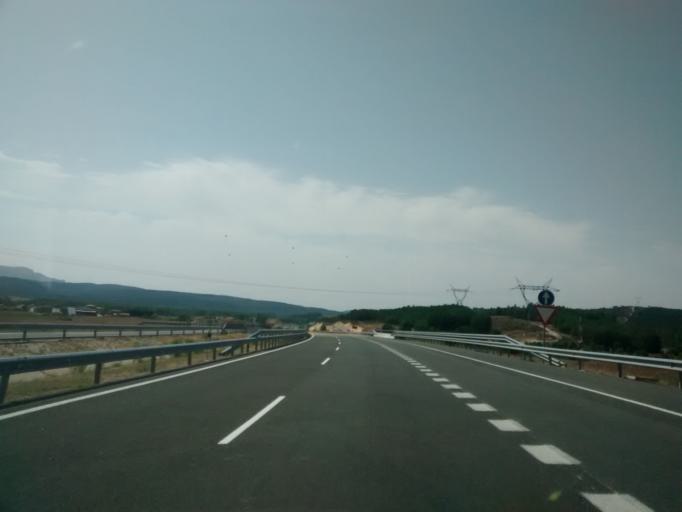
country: ES
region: Castille and Leon
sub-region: Provincia de Palencia
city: Aguilar de Campoo
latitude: 42.7505
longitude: -4.2933
